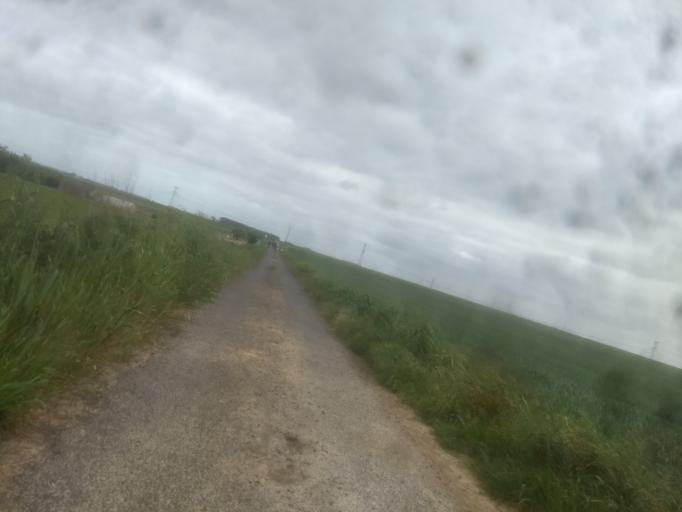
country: FR
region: Nord-Pas-de-Calais
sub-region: Departement du Pas-de-Calais
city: Tilloy-les-Mofflaines
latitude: 50.2689
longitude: 2.8148
